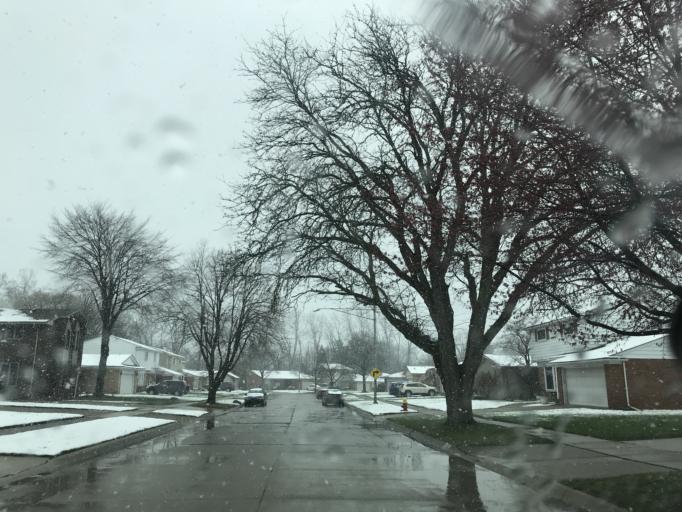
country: US
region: Michigan
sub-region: Wayne County
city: Allen Park
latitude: 42.2333
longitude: -83.2234
